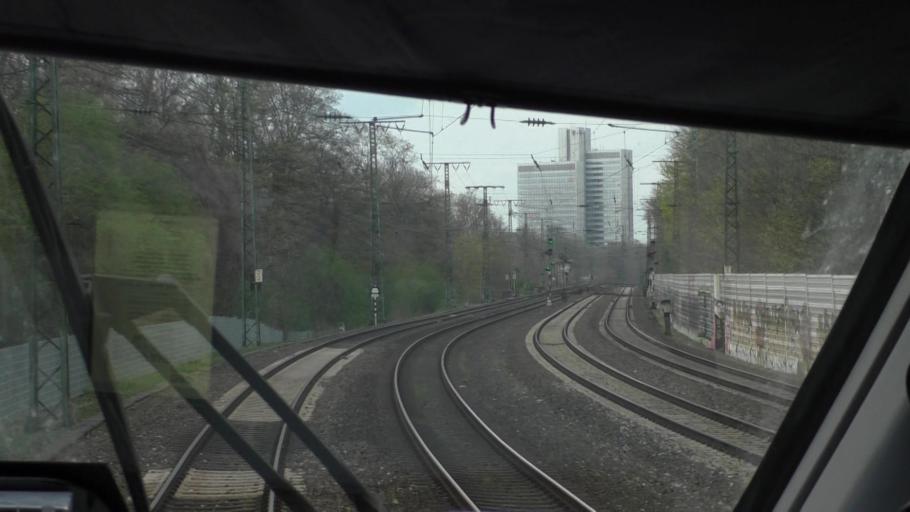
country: DE
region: North Rhine-Westphalia
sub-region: Regierungsbezirk Koln
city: Neustadt/Sued
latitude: 50.9325
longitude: 6.9317
